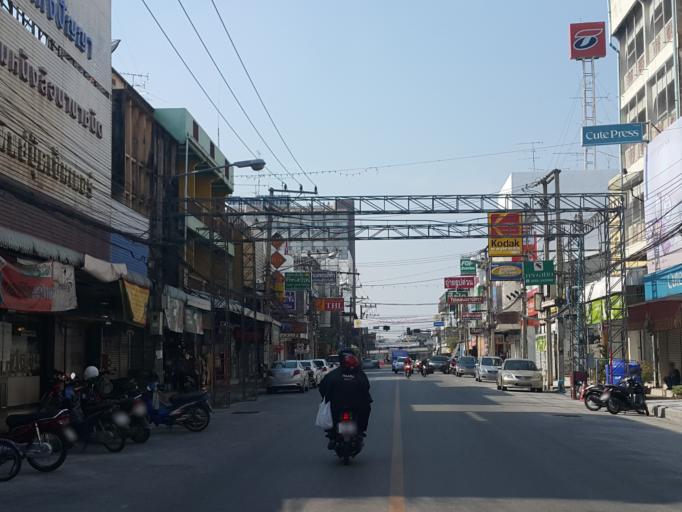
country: TH
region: Phitsanulok
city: Phitsanulok
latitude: 16.8185
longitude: 100.2651
